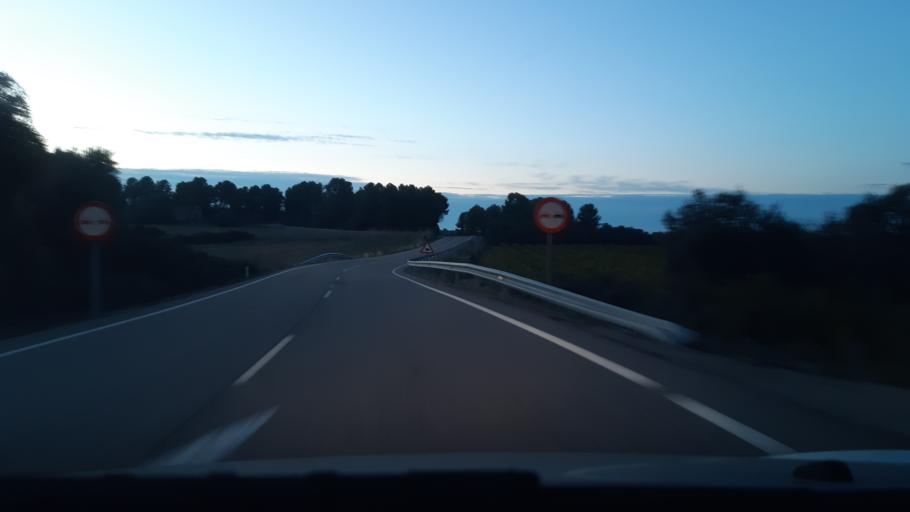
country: ES
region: Aragon
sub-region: Provincia de Teruel
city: Lledo
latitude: 40.9567
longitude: 0.2186
